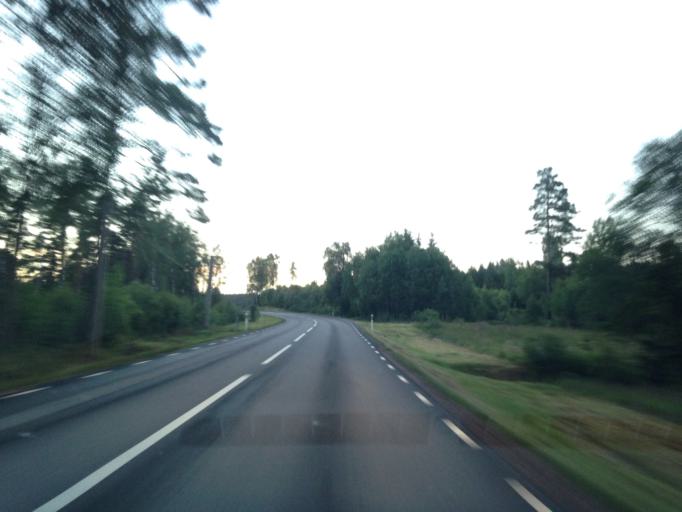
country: SE
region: Vaestra Goetaland
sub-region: Svenljunga Kommun
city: Svenljunga
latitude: 57.5977
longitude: 13.1277
